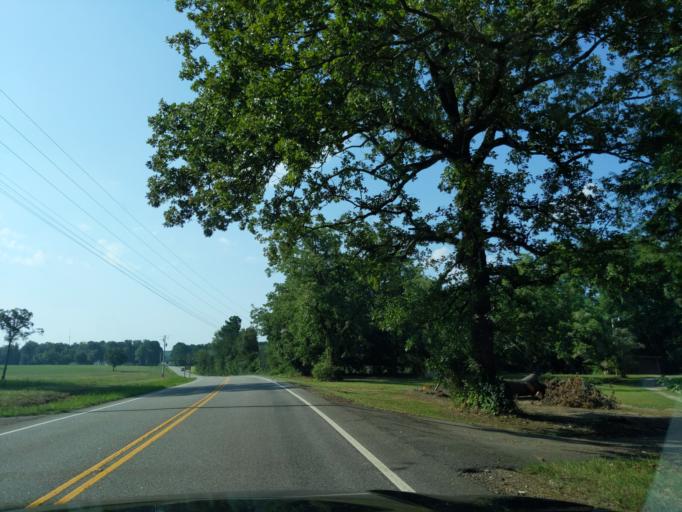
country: US
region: South Carolina
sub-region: Newberry County
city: Prosperity
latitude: 34.0611
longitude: -81.5605
